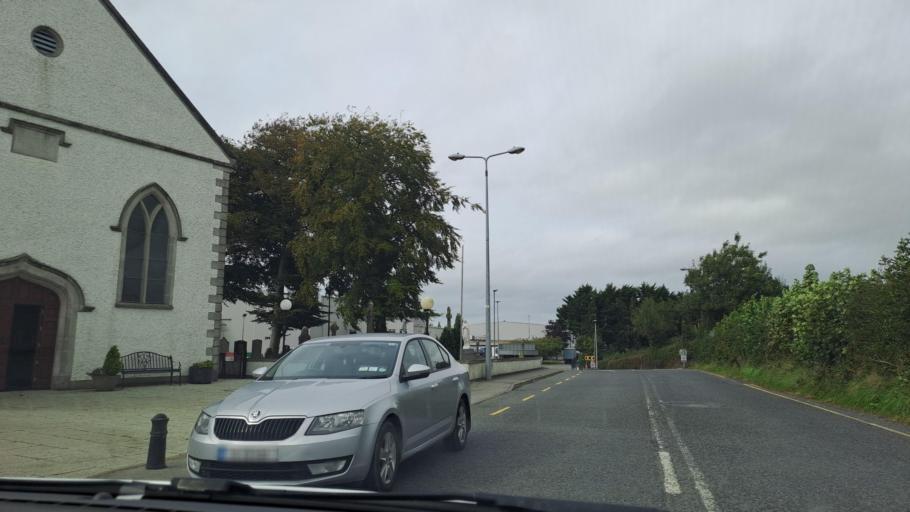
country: IE
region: Ulster
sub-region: An Cabhan
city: Bailieborough
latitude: 53.9965
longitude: -6.9009
